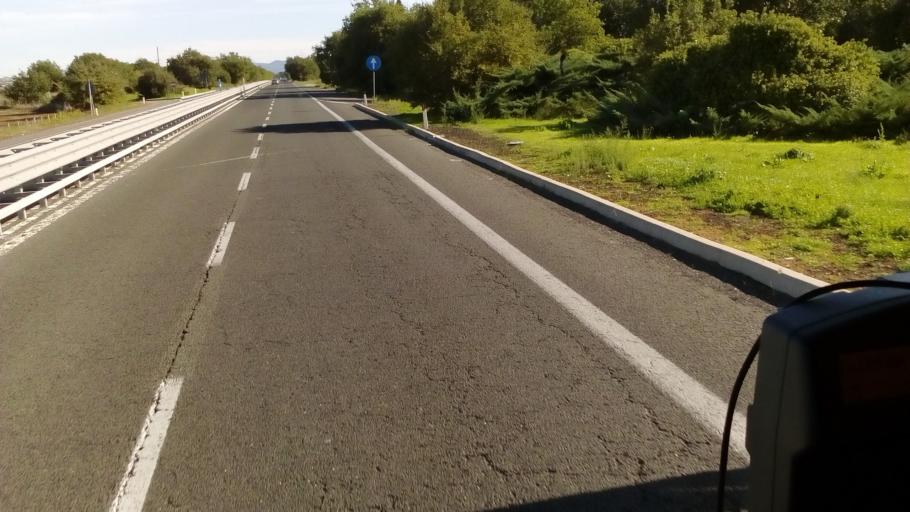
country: IT
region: Latium
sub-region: Provincia di Viterbo
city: Tarquinia
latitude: 42.2928
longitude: 11.6804
